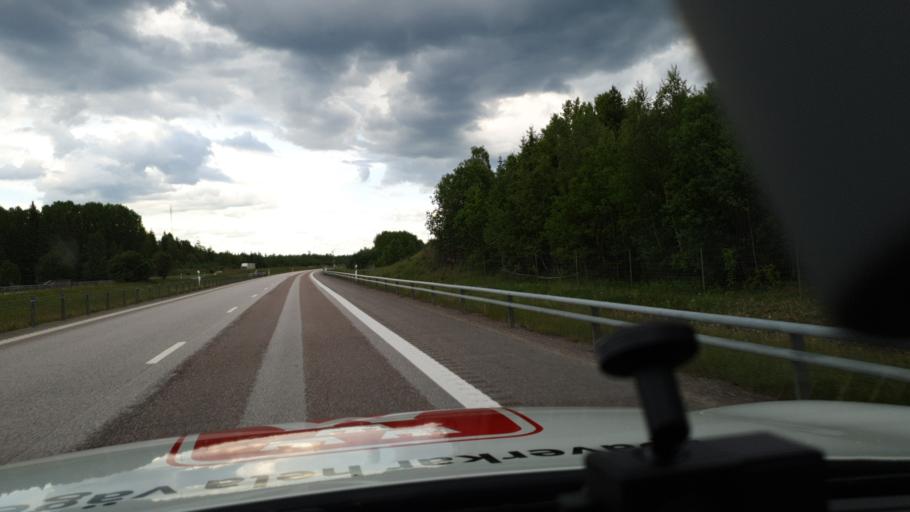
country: SE
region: Uppsala
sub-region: Osthammars Kommun
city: Bjorklinge
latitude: 60.0516
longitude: 17.6202
